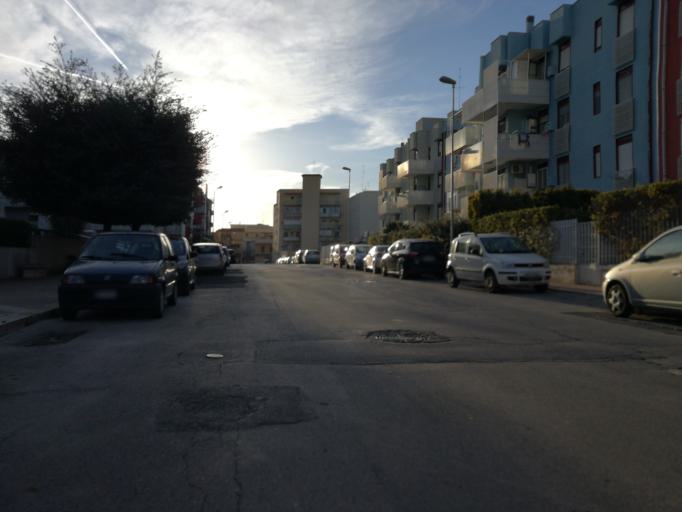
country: IT
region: Apulia
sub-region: Provincia di Bari
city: Valenzano
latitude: 41.0463
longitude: 16.8877
